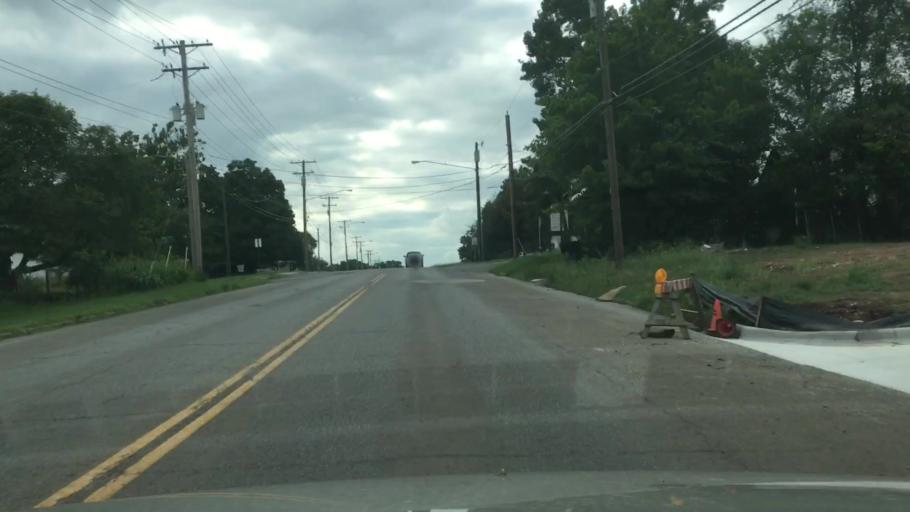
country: US
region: Oklahoma
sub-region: Cherokee County
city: Tahlequah
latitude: 35.9139
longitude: -94.9806
